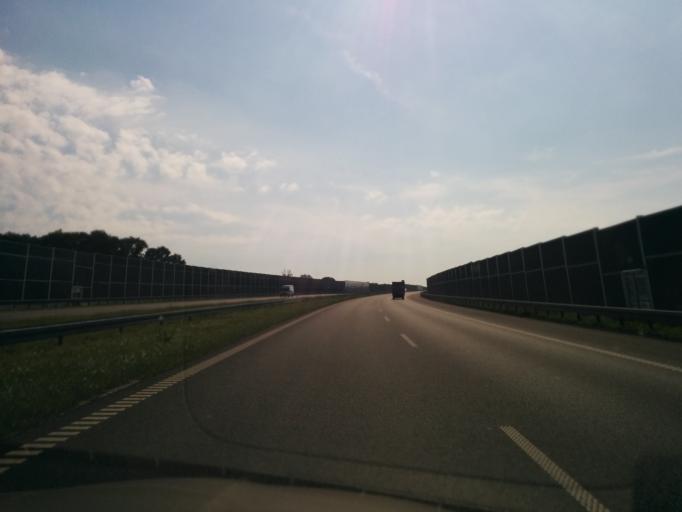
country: PL
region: Silesian Voivodeship
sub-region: Powiat tarnogorski
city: Wieszowa
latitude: 50.3866
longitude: 18.8068
